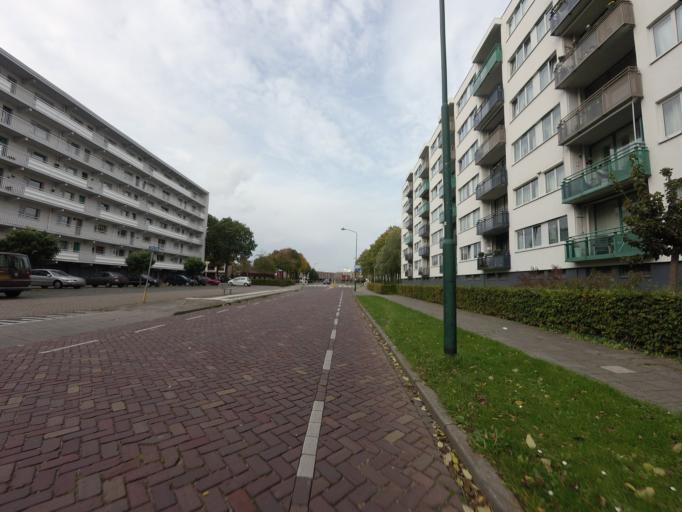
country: NL
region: North Brabant
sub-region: Gemeente Breda
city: Breda
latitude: 51.5877
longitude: 4.7503
